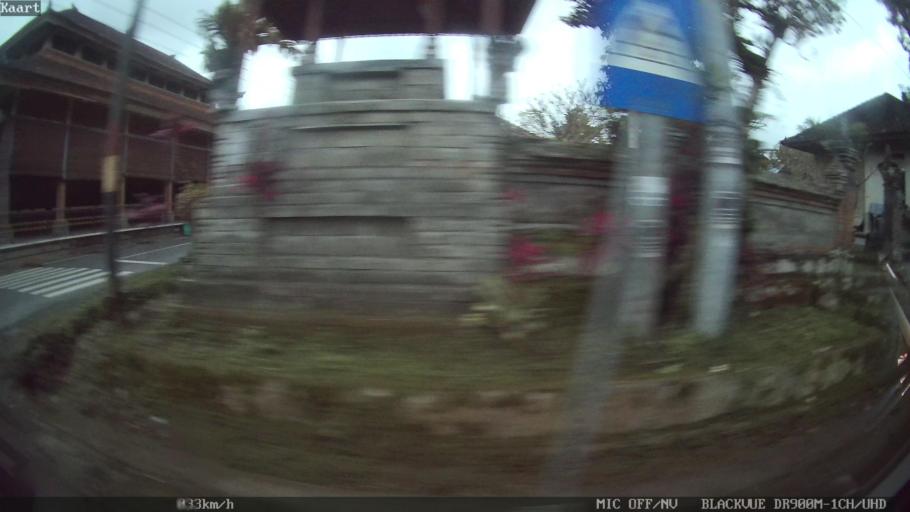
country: ID
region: Bali
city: Banjar Tengah
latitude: -8.4489
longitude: 115.2773
